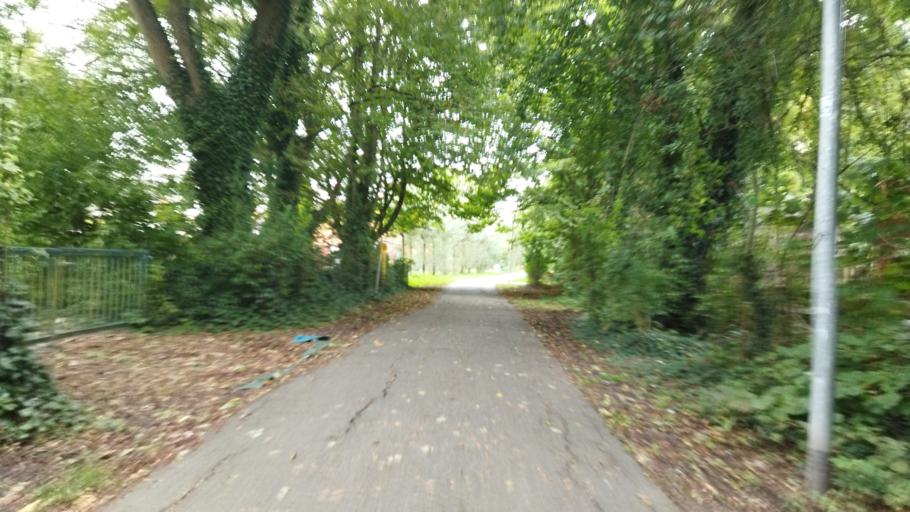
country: DE
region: Lower Saxony
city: Leer
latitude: 53.2226
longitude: 7.4413
